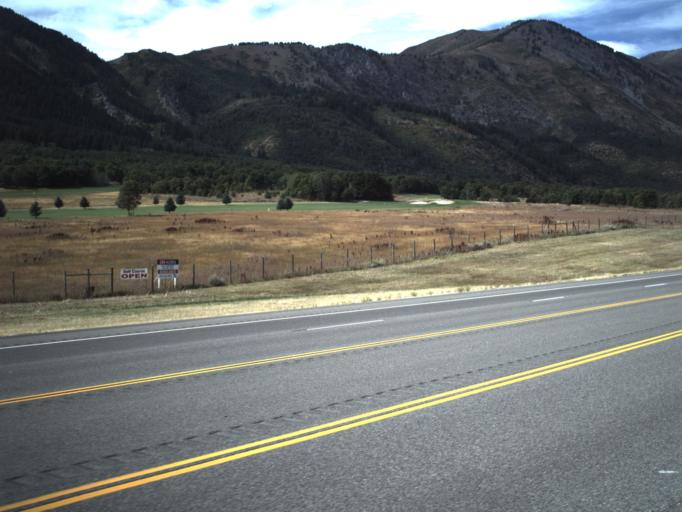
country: US
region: Utah
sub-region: Cache County
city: Wellsville
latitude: 41.5849
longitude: -111.9753
